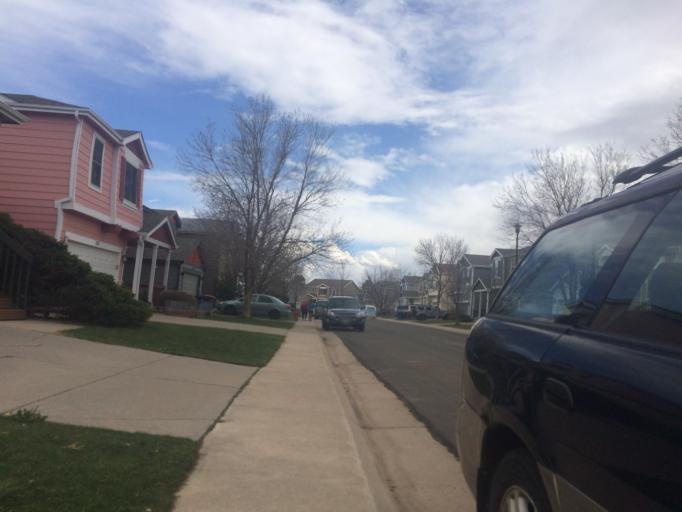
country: US
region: Colorado
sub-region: Boulder County
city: Superior
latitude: 39.9569
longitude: -105.1779
